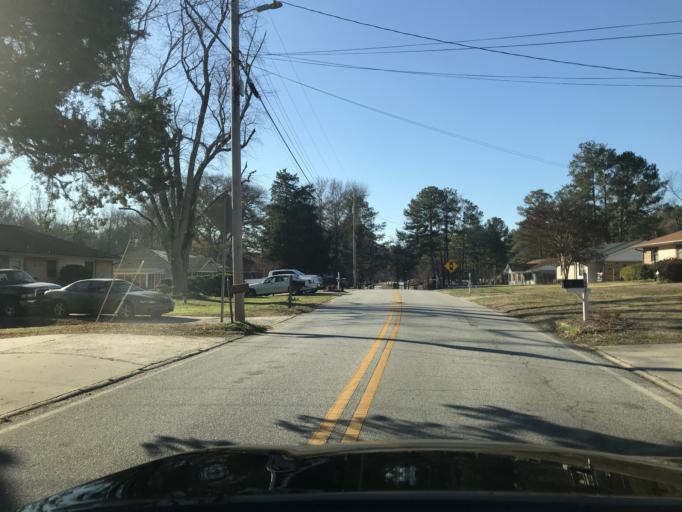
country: US
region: Georgia
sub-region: Clayton County
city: Jonesboro
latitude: 33.5562
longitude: -84.3631
